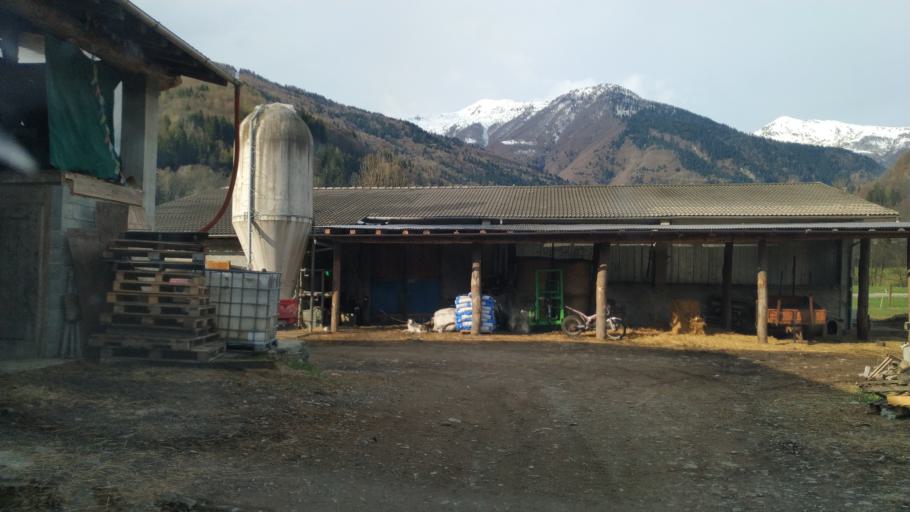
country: IT
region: Piedmont
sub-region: Provincia di Vercelli
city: Scopello
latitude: 45.7764
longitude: 8.1041
